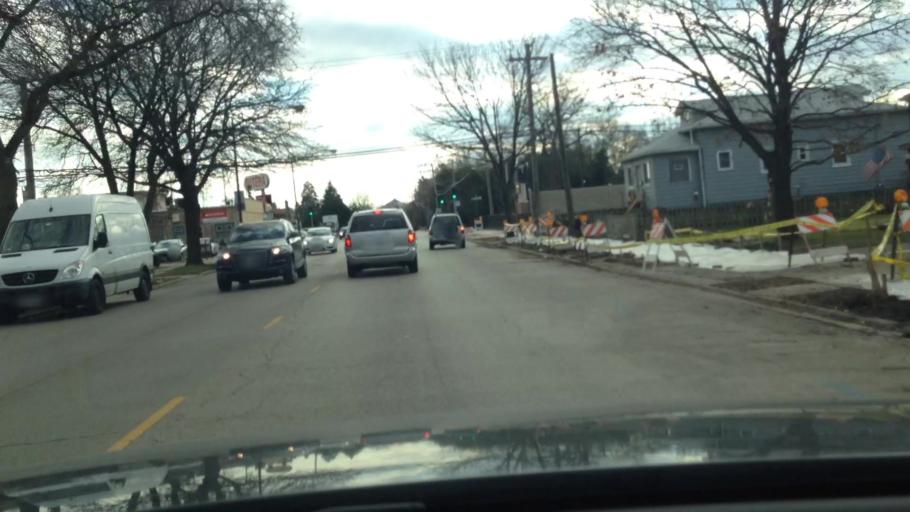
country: US
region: Illinois
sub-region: Cook County
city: Harwood Heights
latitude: 41.9693
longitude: -87.7880
